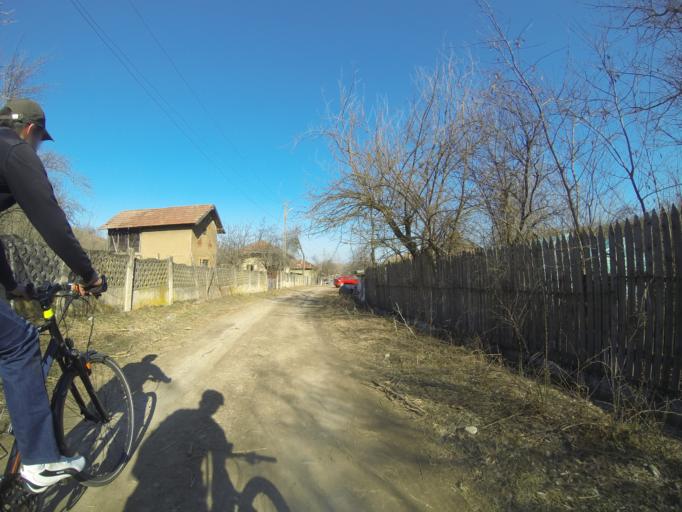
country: RO
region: Dolj
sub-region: Comuna Teascu
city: Teasc
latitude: 44.1484
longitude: 23.8341
